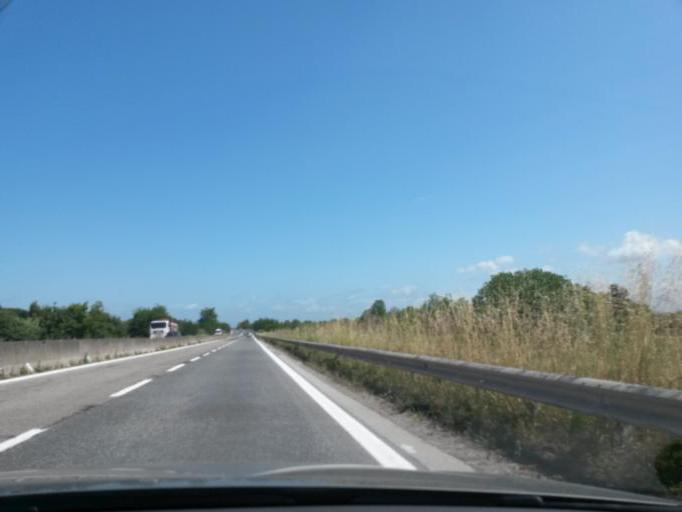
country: IT
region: Tuscany
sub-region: Provincia di Livorno
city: Donoratico
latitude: 43.1422
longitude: 10.5523
